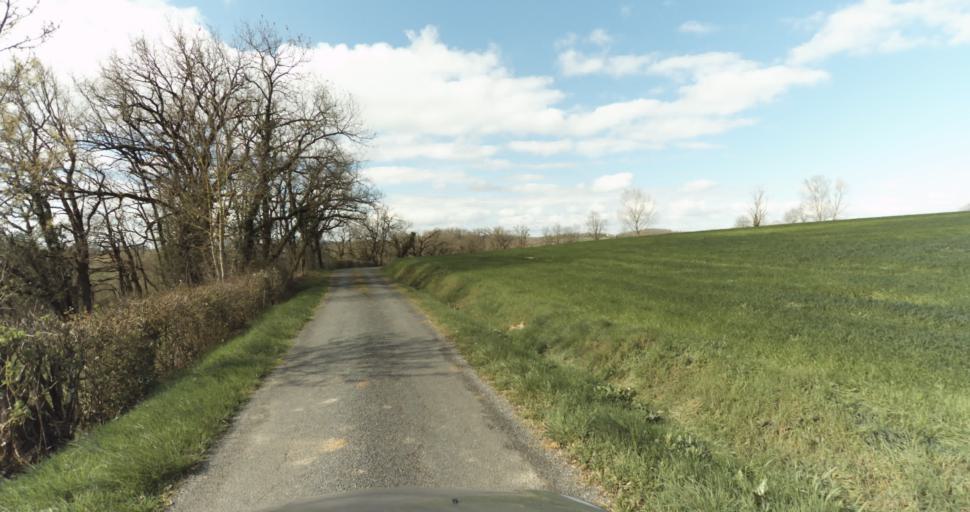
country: FR
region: Midi-Pyrenees
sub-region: Departement du Tarn
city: Frejairolles
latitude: 43.8577
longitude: 2.1985
